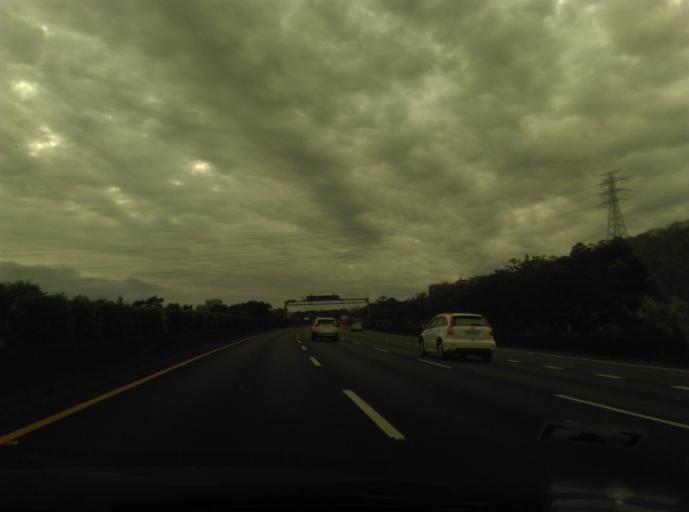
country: TW
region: Taiwan
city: Daxi
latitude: 24.9124
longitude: 121.2928
